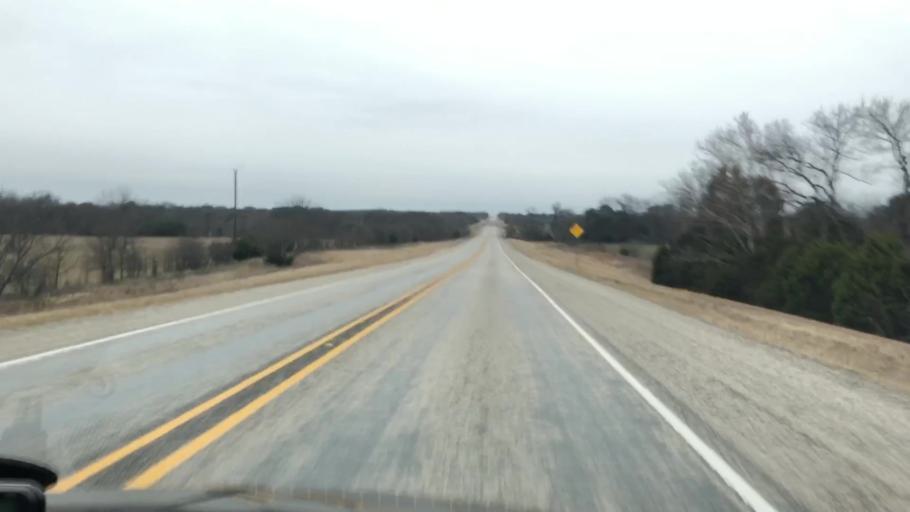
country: US
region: Texas
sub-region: Lampasas County
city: Lampasas
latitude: 31.2111
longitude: -98.1725
